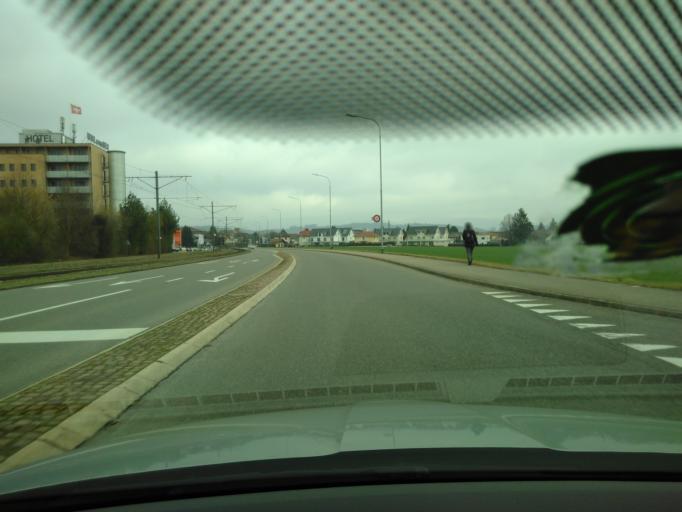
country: CH
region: Aargau
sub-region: Bezirk Aarau
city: Oberentfelden
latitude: 47.3495
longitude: 8.0497
